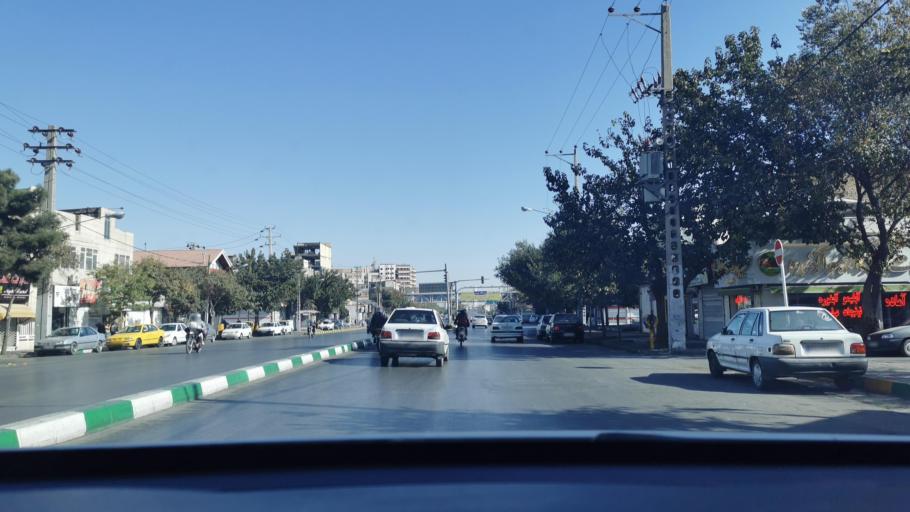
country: IR
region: Razavi Khorasan
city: Mashhad
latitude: 36.3215
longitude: 59.6206
